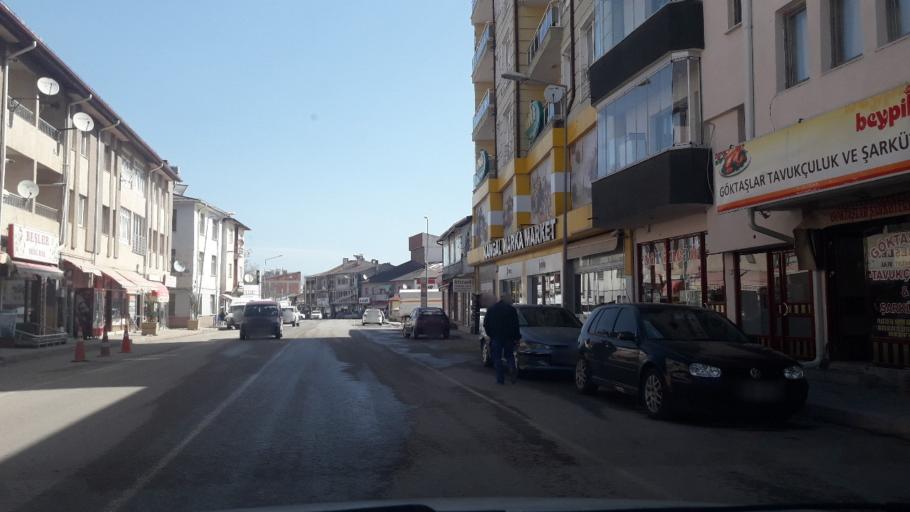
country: TR
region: Sivas
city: Kangal
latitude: 39.2334
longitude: 37.3905
